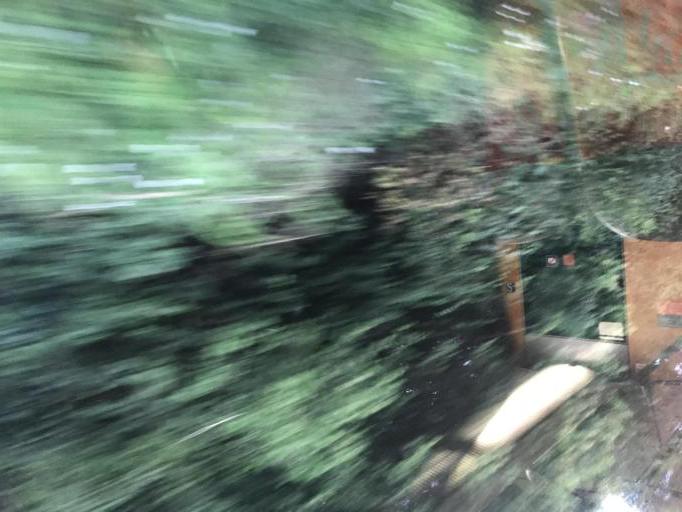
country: DE
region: Rheinland-Pfalz
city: Brachbach
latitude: 50.8219
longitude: 7.9234
